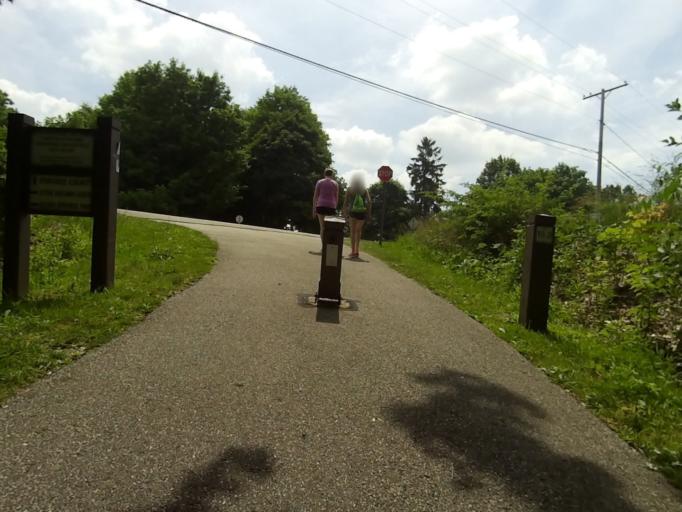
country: US
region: Ohio
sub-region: Summit County
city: Stow
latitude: 41.1909
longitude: -81.4023
